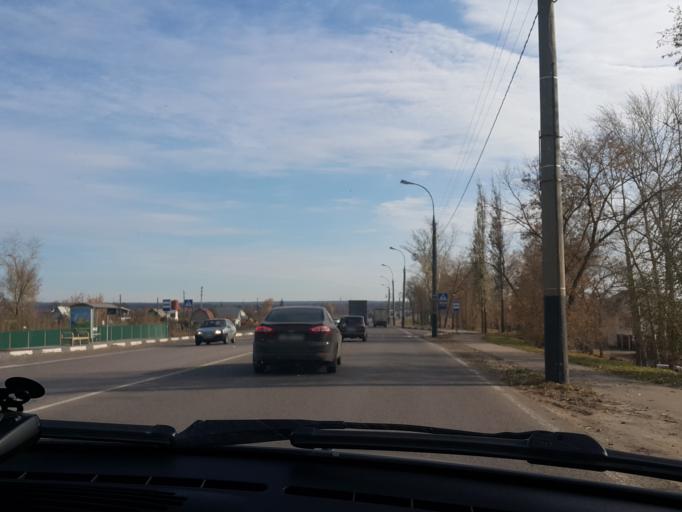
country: RU
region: Tambov
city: Tambov
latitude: 52.7222
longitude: 41.4829
